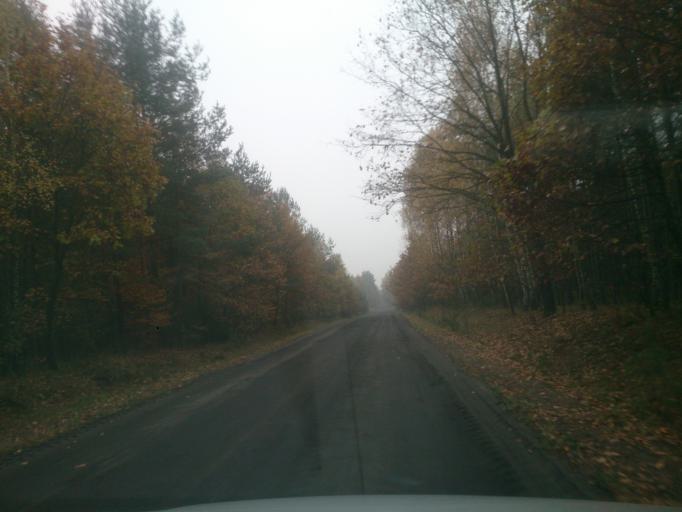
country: PL
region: Kujawsko-Pomorskie
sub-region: Powiat golubsko-dobrzynski
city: Golub-Dobrzyn
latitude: 53.1570
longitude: 19.1284
